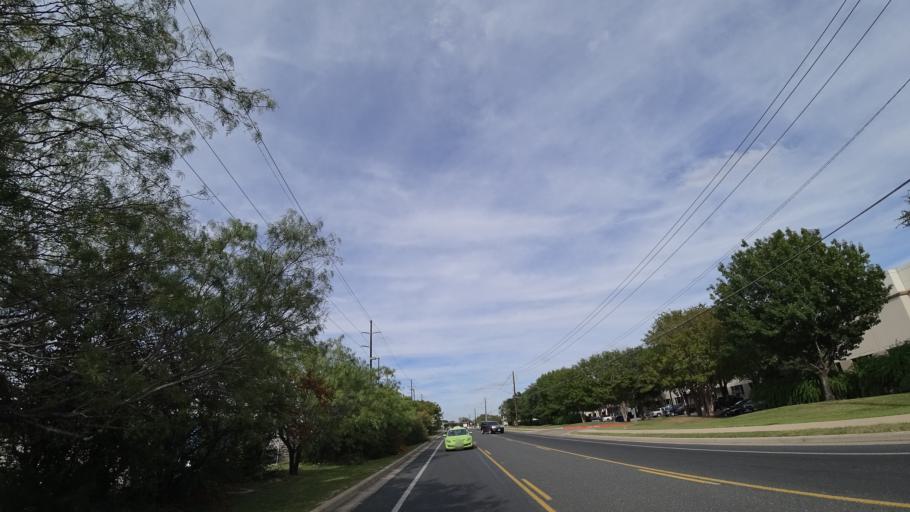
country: US
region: Texas
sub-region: Travis County
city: Austin
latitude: 30.2084
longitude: -97.7507
